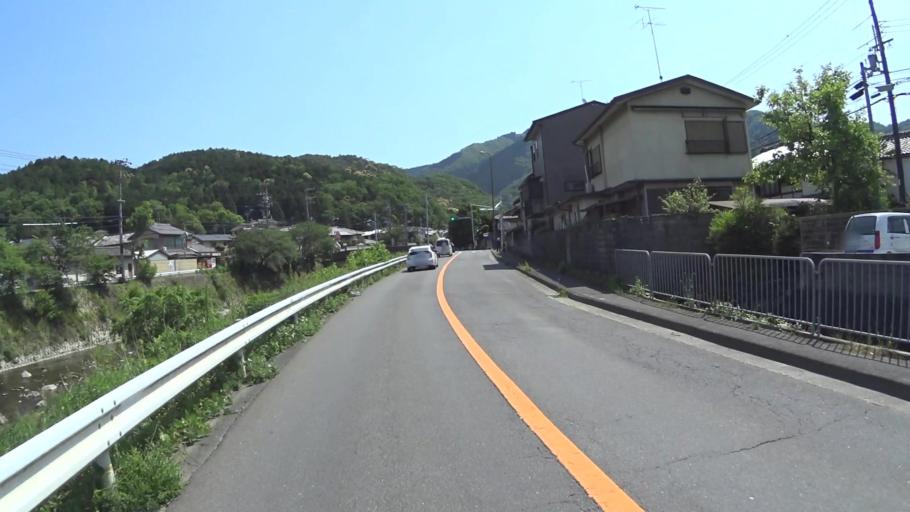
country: JP
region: Kyoto
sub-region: Kyoto-shi
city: Kamigyo-ku
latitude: 35.0623
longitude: 135.7946
